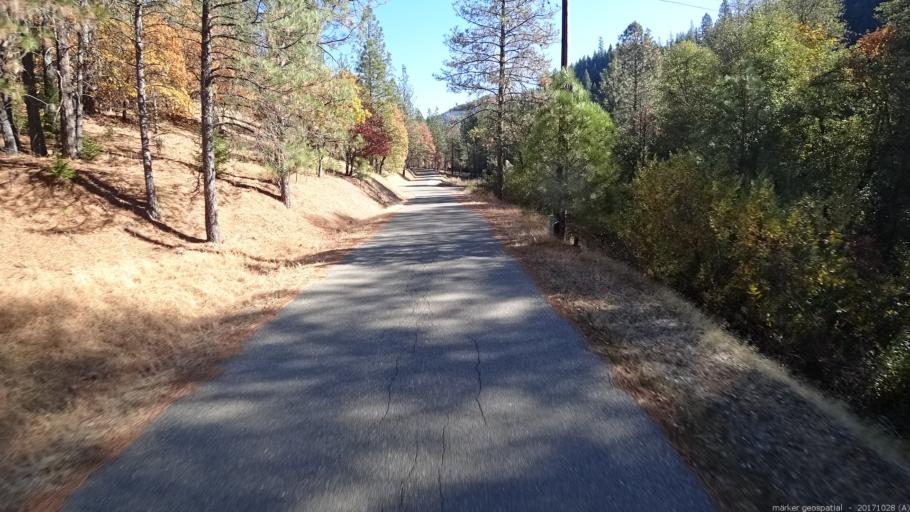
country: US
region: California
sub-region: Shasta County
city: Shasta
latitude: 40.7635
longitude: -122.5647
